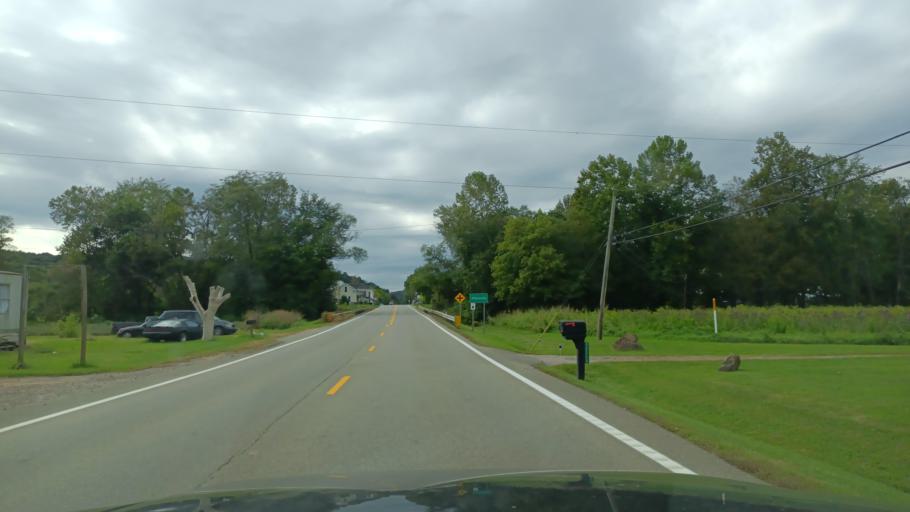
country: US
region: Ohio
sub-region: Vinton County
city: McArthur
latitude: 39.2725
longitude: -82.6034
